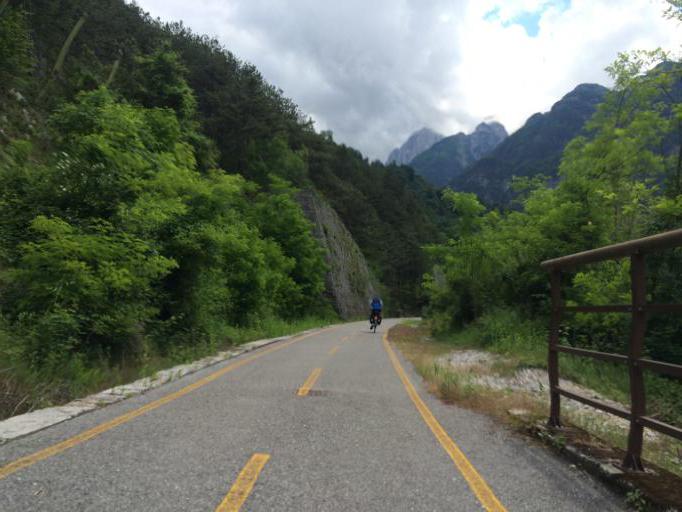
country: IT
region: Friuli Venezia Giulia
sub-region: Provincia di Udine
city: Dogna
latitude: 46.4561
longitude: 13.3115
